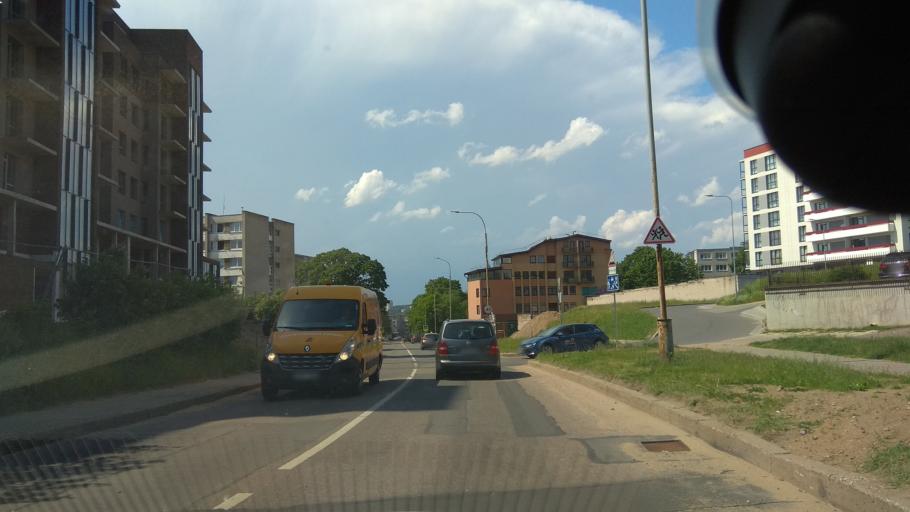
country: LT
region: Vilnius County
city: Vilkpede
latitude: 54.6687
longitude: 25.2491
